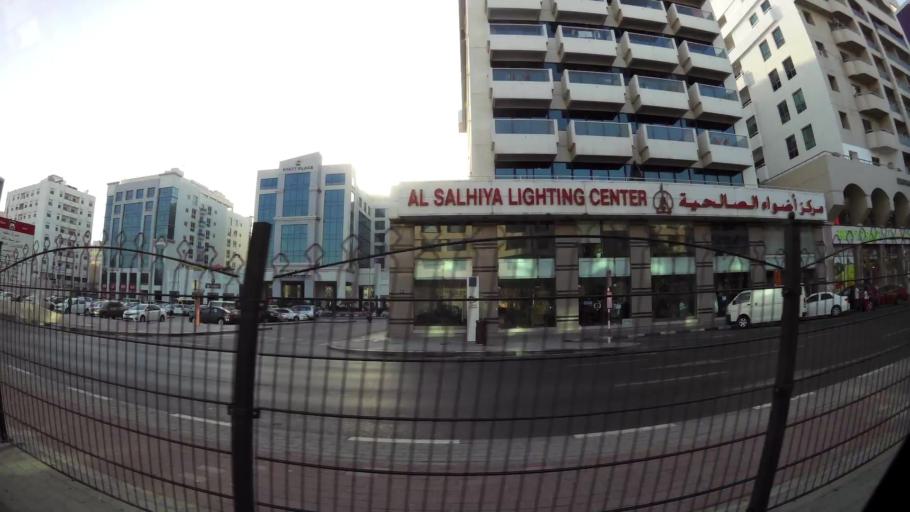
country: AE
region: Ash Shariqah
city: Sharjah
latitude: 25.2628
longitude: 55.3288
